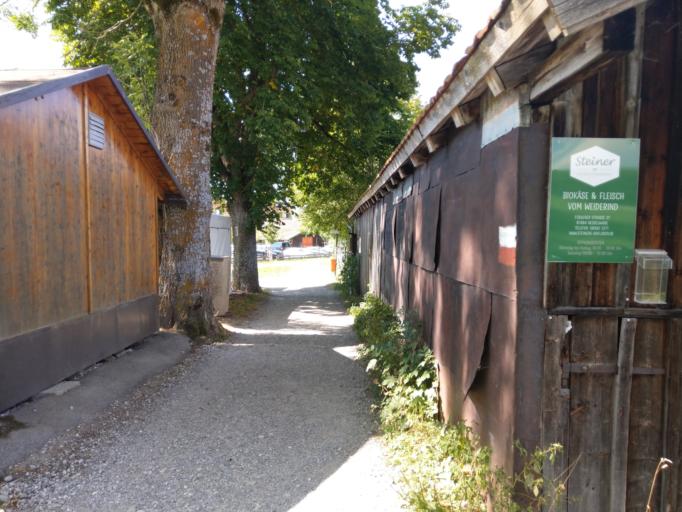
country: DE
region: Bavaria
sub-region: Swabia
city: Nesselwang
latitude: 47.6175
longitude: 10.5021
